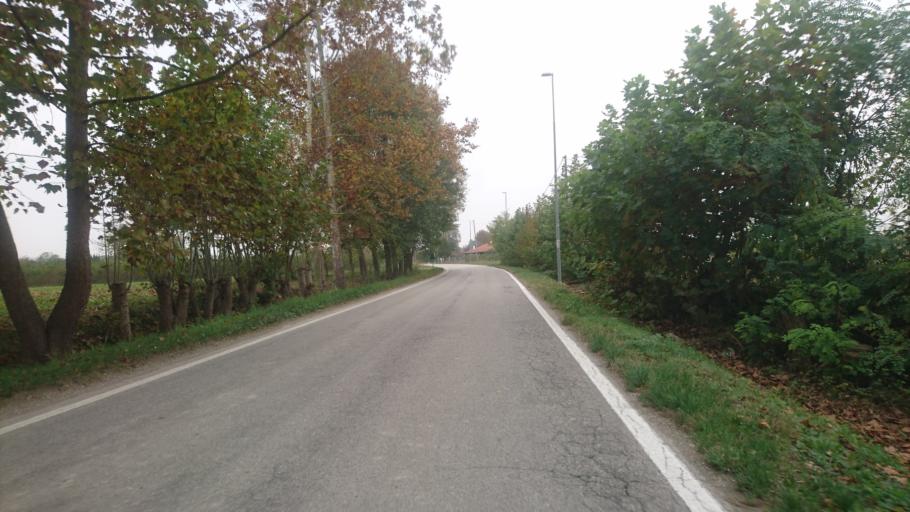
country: IT
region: Veneto
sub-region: Provincia di Venezia
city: Tombelle
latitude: 45.3867
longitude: 11.9820
